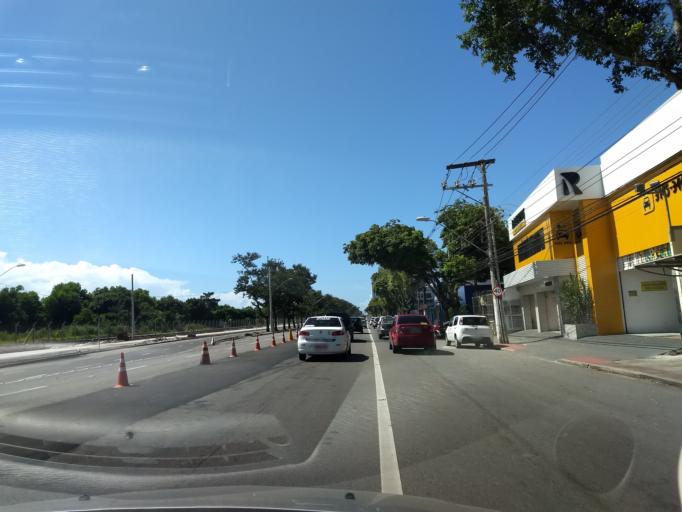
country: BR
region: Espirito Santo
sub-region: Vila Velha
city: Vila Velha
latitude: -20.2670
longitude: -40.2953
